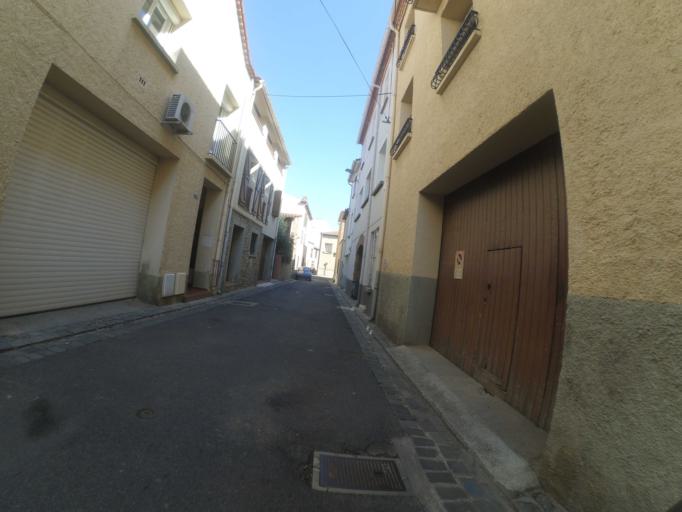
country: FR
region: Languedoc-Roussillon
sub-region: Departement des Pyrenees-Orientales
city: Thuir
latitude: 42.6335
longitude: 2.7577
